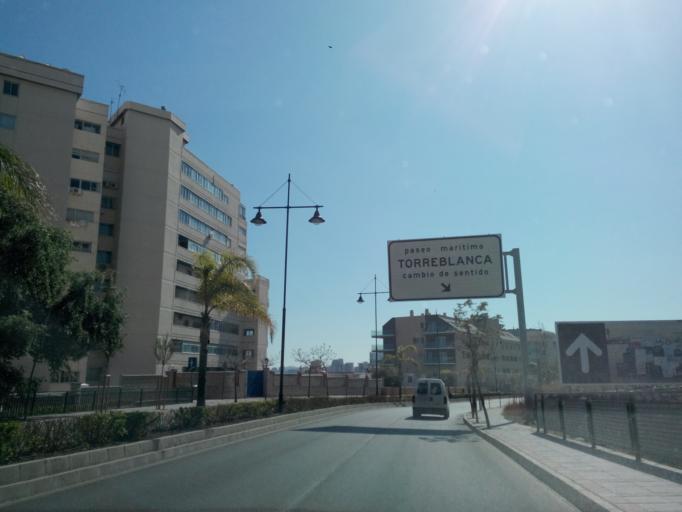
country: ES
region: Andalusia
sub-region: Provincia de Malaga
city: Fuengirola
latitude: 36.5648
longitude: -4.6011
